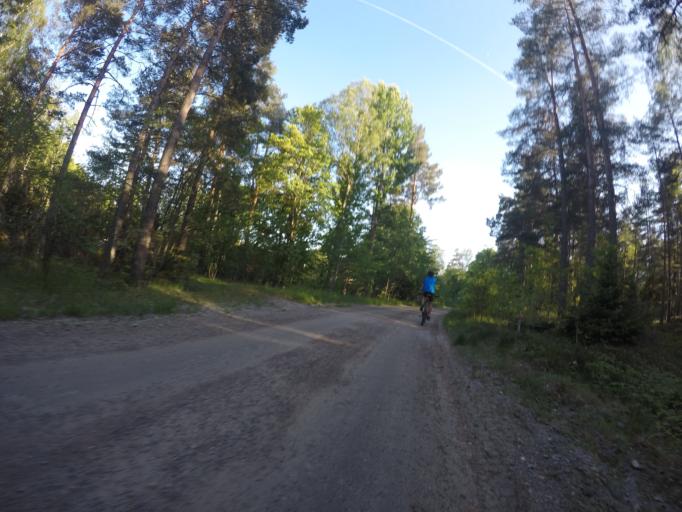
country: SE
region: Soedermanland
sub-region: Eskilstuna Kommun
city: Eskilstuna
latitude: 59.3486
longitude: 16.5340
